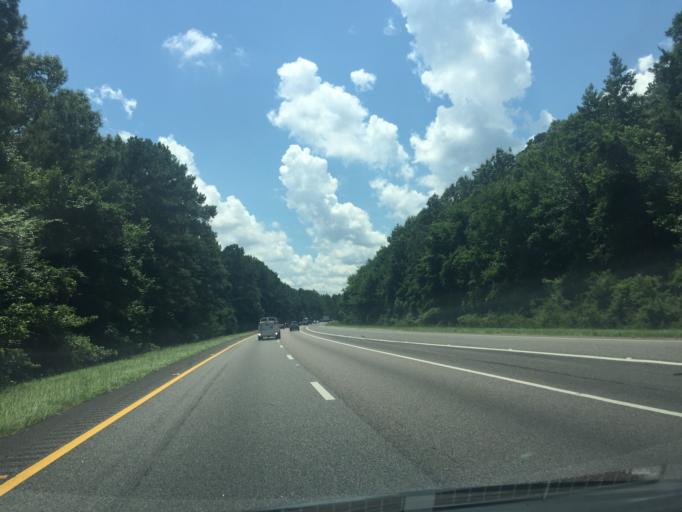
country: US
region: South Carolina
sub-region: Jasper County
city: Hardeeville
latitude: 32.2577
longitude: -81.0993
